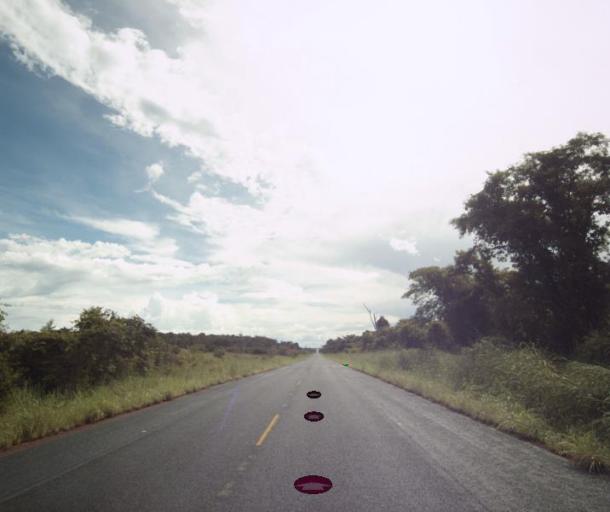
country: BR
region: Goias
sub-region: Sao Miguel Do Araguaia
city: Sao Miguel do Araguaia
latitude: -13.2998
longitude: -50.3076
